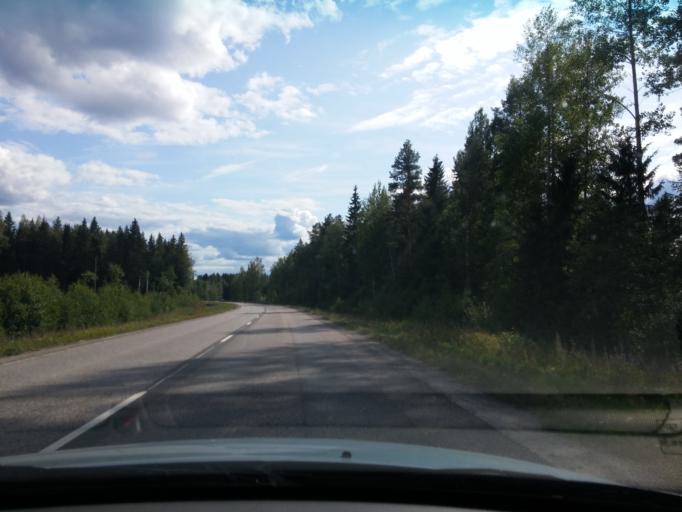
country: FI
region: Central Finland
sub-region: Keuruu
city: Keuruu
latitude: 62.2770
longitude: 24.6885
